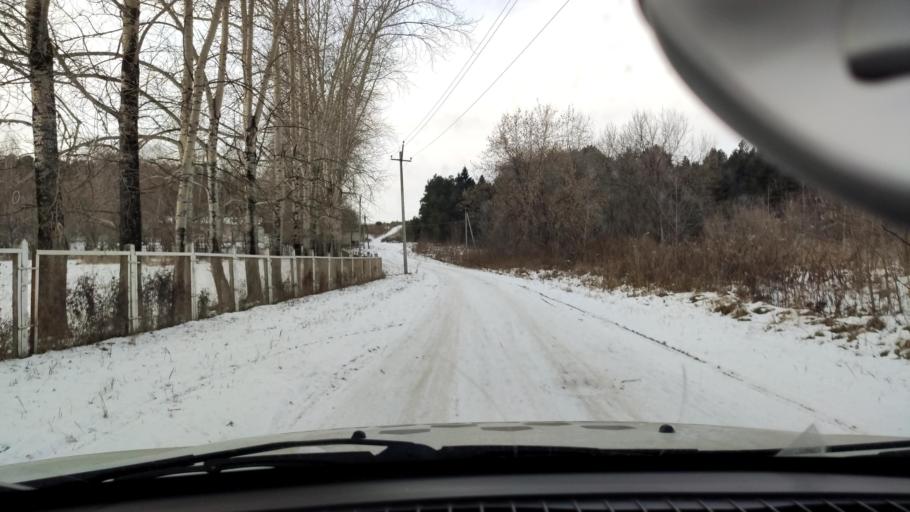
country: RU
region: Perm
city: Lobanovo
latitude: 57.8263
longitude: 56.3531
